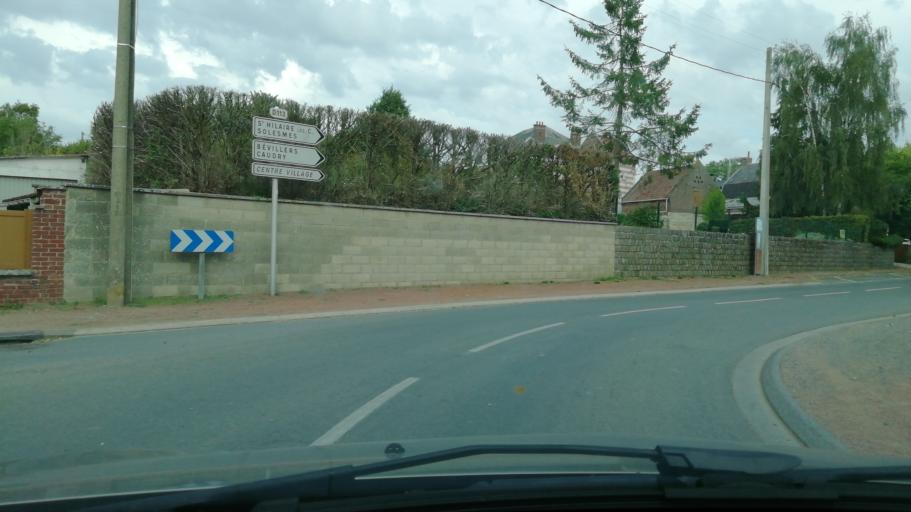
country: FR
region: Nord-Pas-de-Calais
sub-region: Departement du Nord
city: Beauvois-en-Cambresis
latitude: 50.1655
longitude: 3.3631
